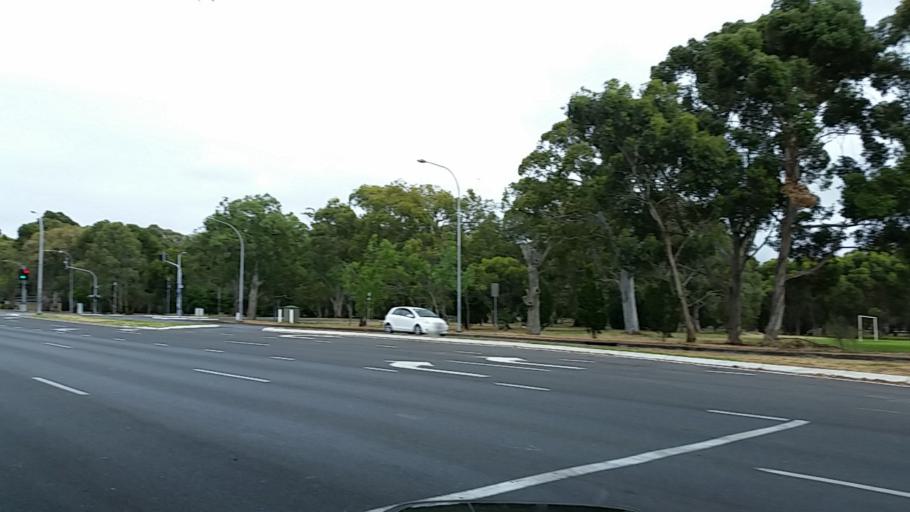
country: AU
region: South Australia
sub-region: Unley
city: Unley
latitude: -34.9410
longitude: 138.6078
